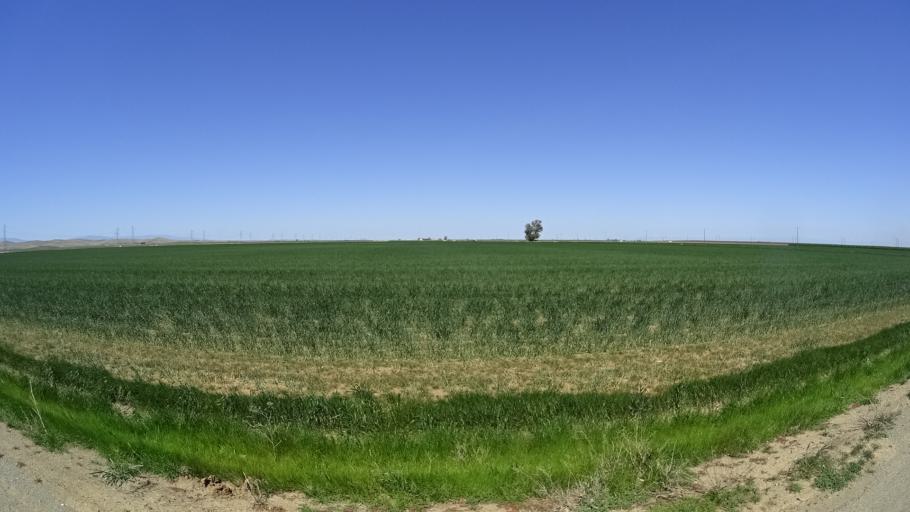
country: US
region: California
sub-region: Glenn County
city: Willows
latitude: 39.4656
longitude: -122.2780
